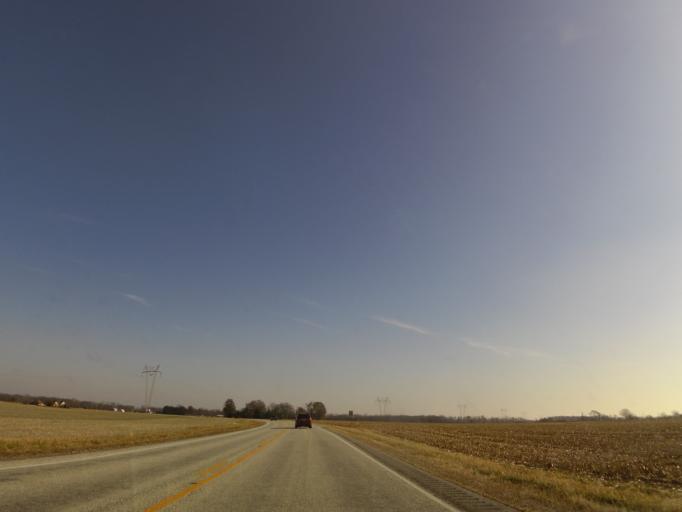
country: US
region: Indiana
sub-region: Shelby County
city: Morristown
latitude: 39.5730
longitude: -85.5970
